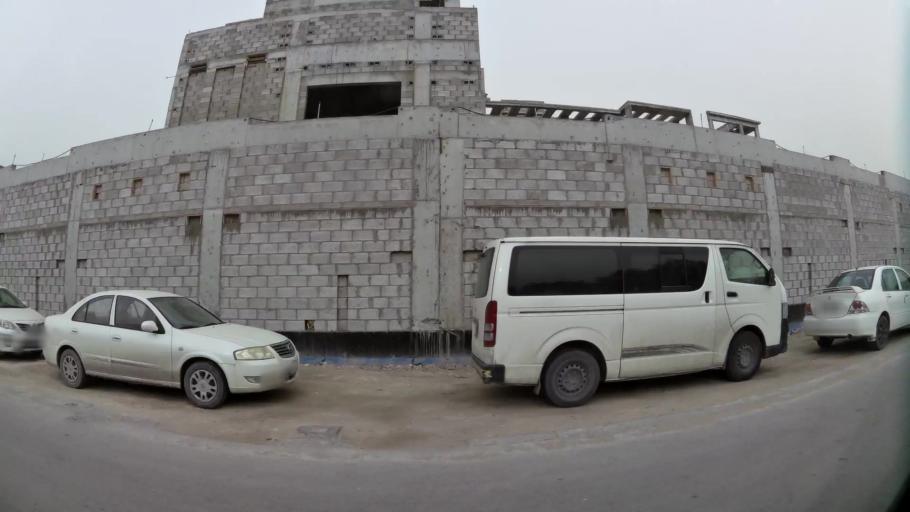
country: QA
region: Baladiyat ad Dawhah
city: Doha
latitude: 25.2590
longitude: 51.4942
